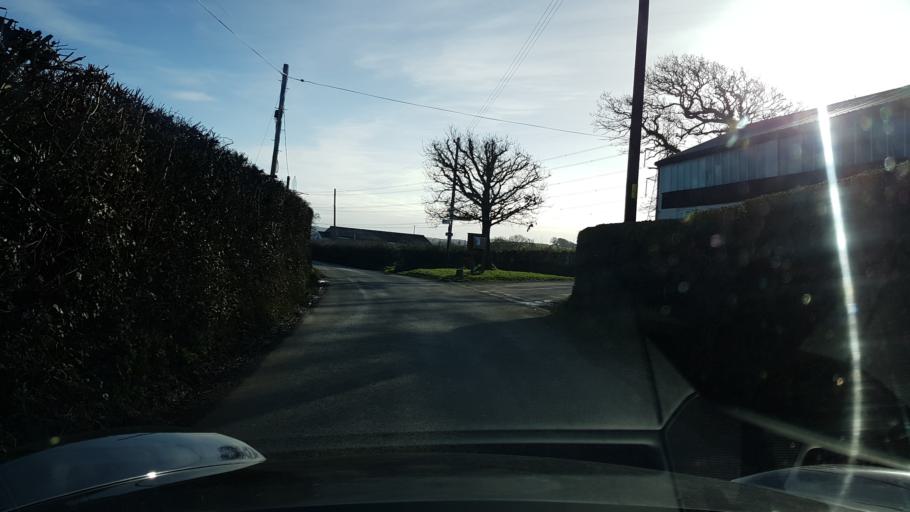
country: GB
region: England
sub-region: Dorset
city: Bridport
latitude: 50.7649
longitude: -2.8001
